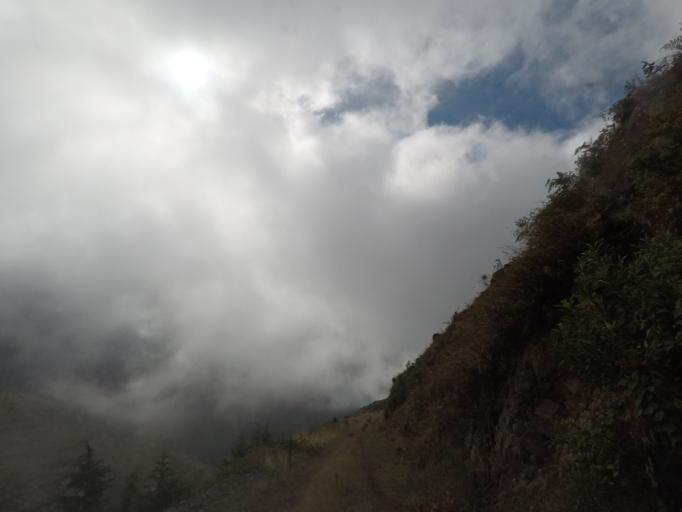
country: PT
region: Madeira
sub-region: Funchal
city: Nossa Senhora do Monte
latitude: 32.6974
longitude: -16.9124
